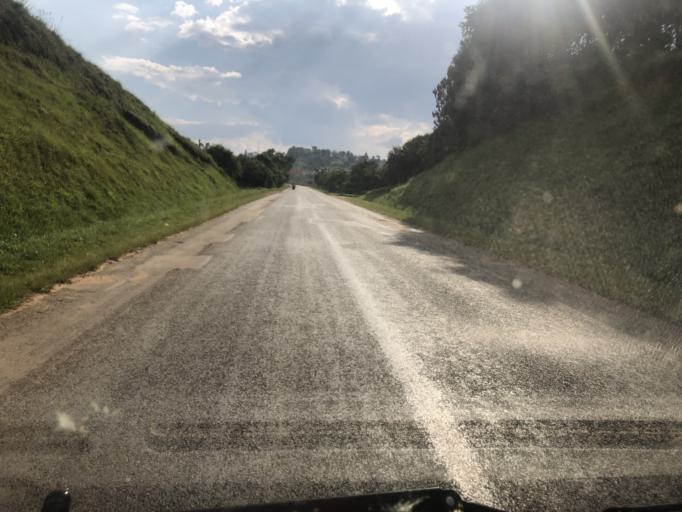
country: UG
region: Western Region
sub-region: Bushenyi District
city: Bushenyi
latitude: -0.5434
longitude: 30.2128
